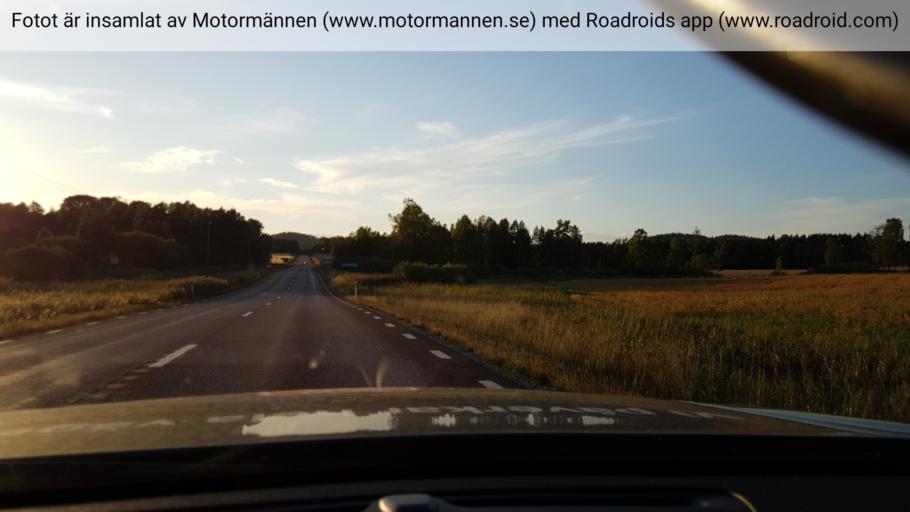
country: SE
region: OErebro
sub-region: Karlskoga Kommun
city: Karlskoga
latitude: 59.4374
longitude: 14.4082
